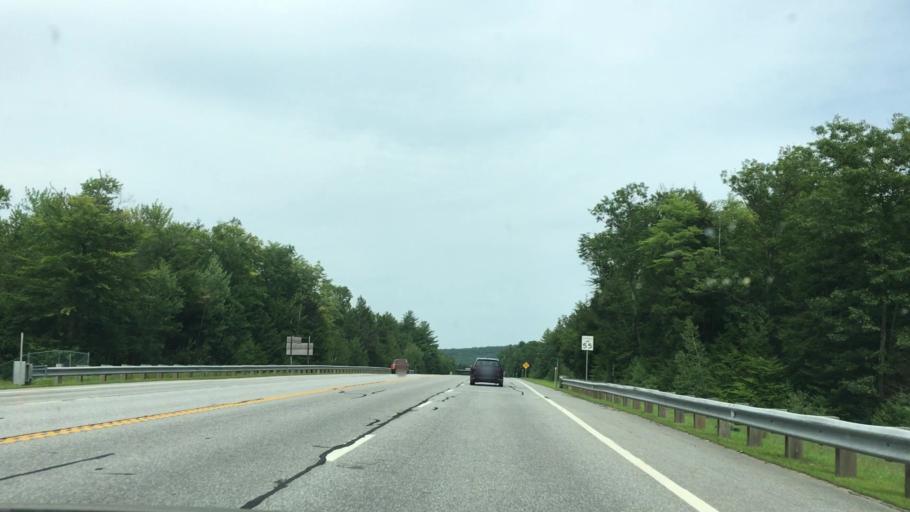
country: US
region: New Hampshire
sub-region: Hillsborough County
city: Hillsborough
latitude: 43.1187
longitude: -71.9087
